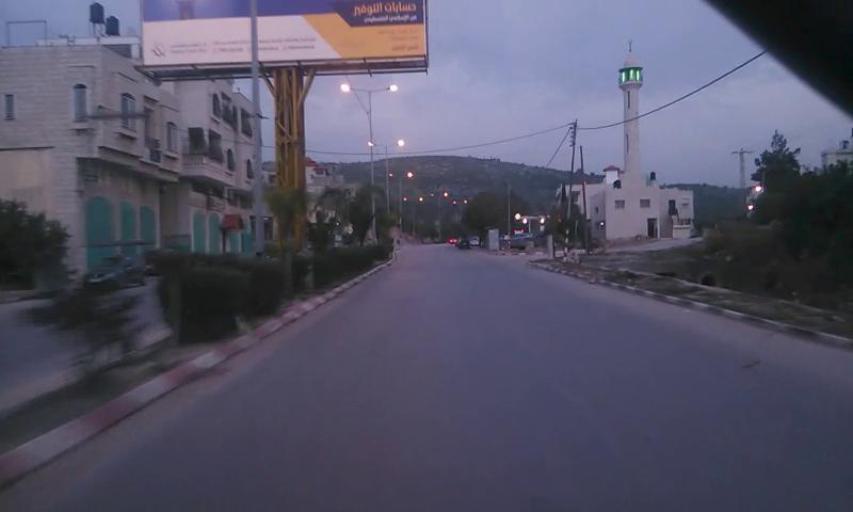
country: PS
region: West Bank
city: `Anabta
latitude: 32.3038
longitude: 35.1265
